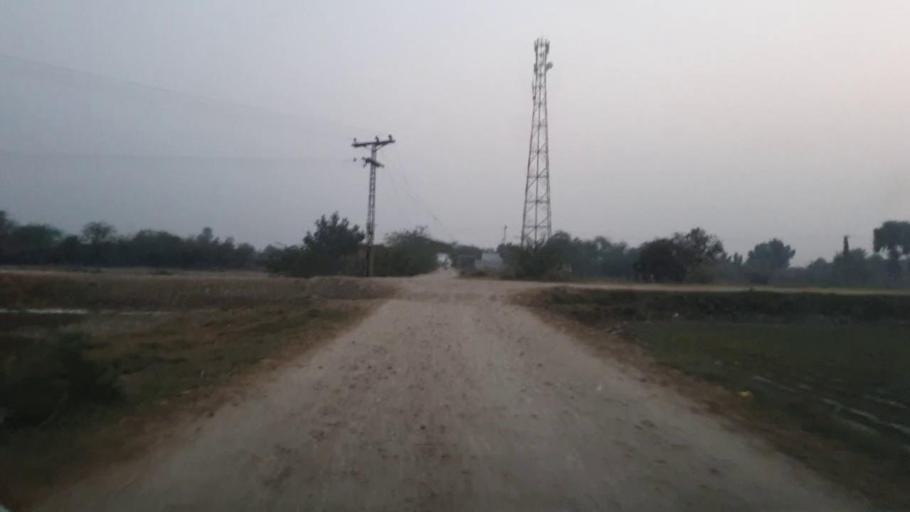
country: PK
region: Sindh
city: Karaundi
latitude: 26.9232
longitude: 68.4299
